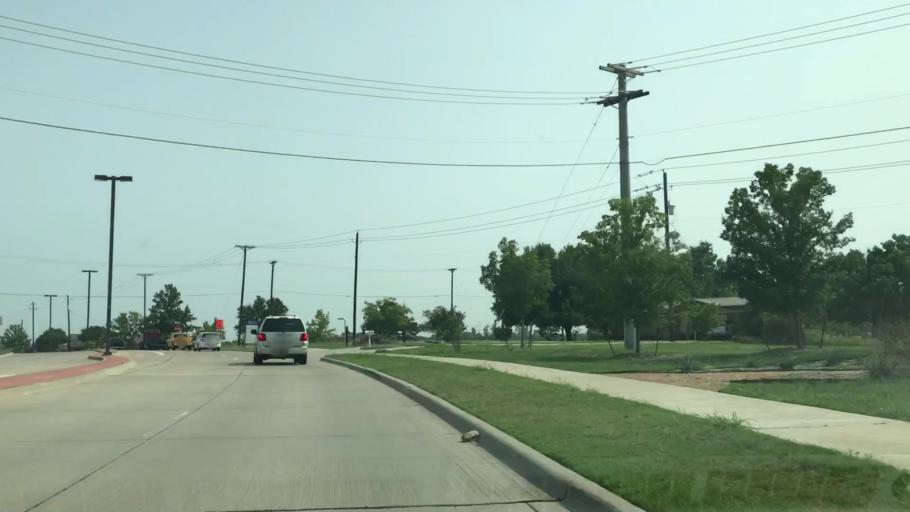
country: US
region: Texas
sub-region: Dallas County
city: Rowlett
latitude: 32.9424
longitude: -96.5695
